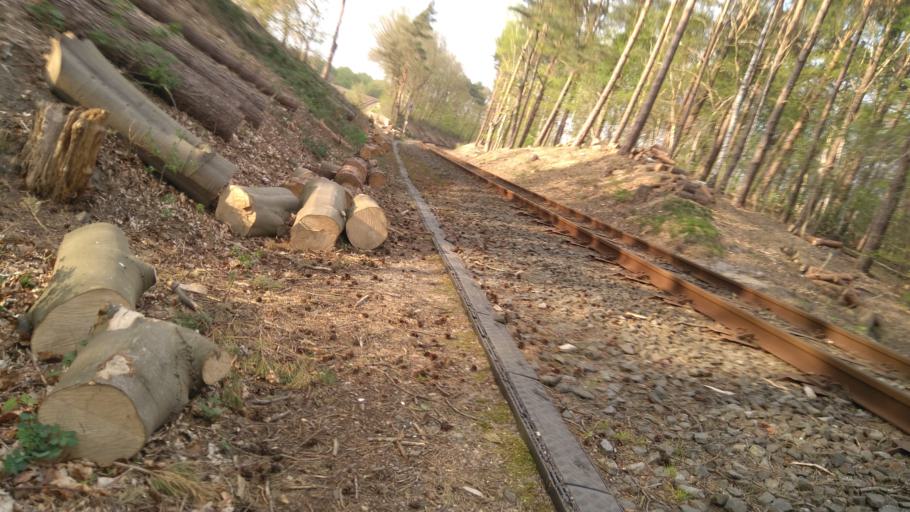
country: DE
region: Lower Saxony
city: Buxtehude
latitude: 53.4638
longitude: 9.6542
